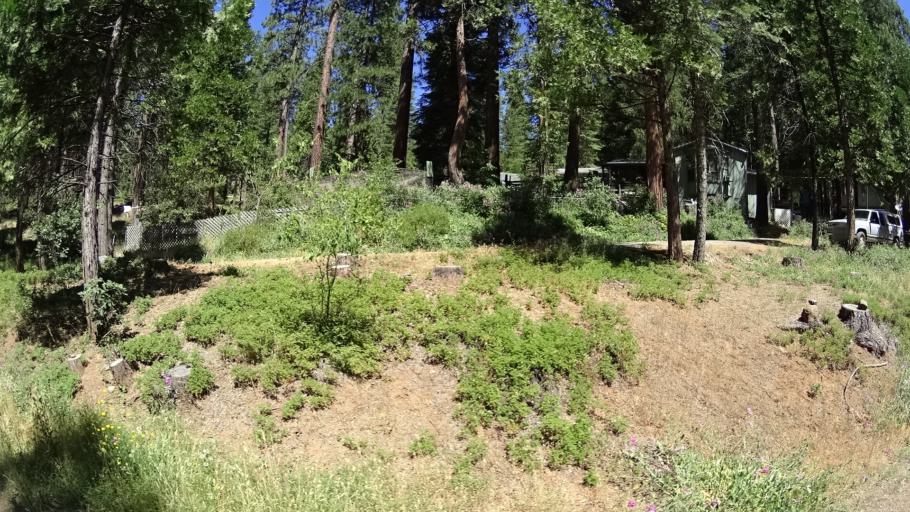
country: US
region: California
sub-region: Amador County
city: Pioneer
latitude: 38.4388
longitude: -120.4329
